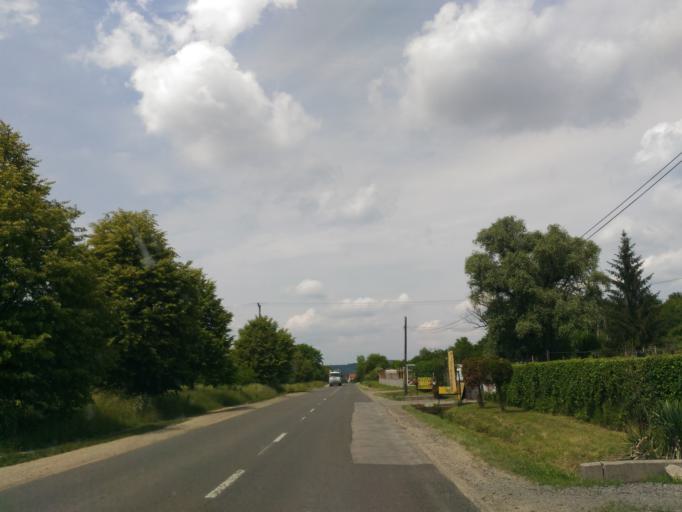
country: HU
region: Baranya
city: Komlo
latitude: 46.2053
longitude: 18.2486
